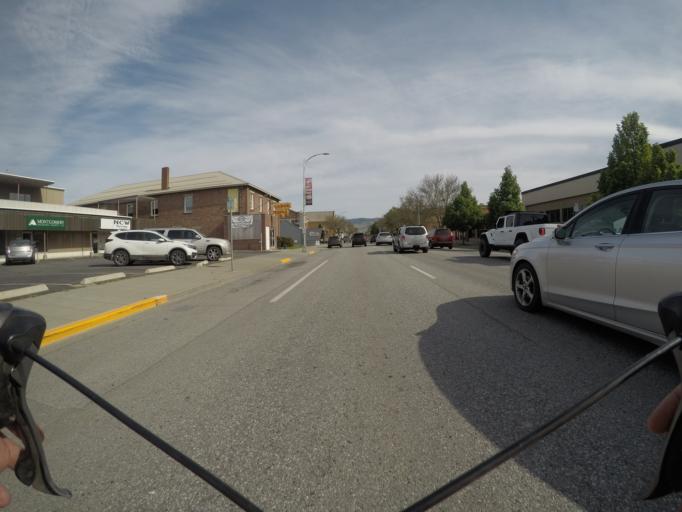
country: US
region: Washington
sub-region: Chelan County
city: Wenatchee
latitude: 47.4249
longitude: -120.3148
